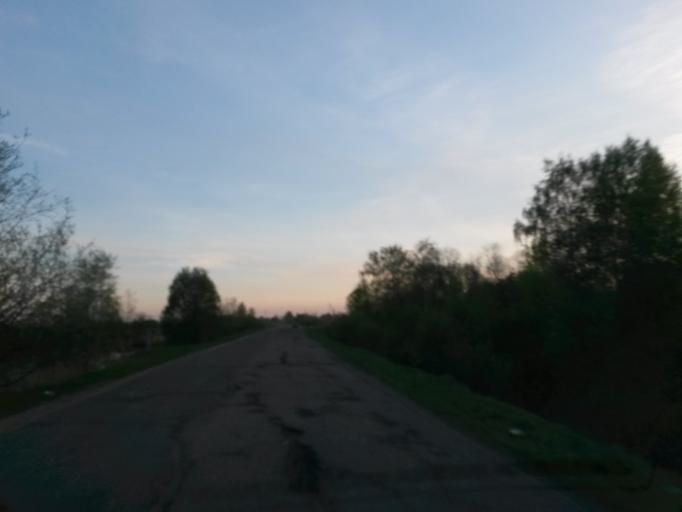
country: RU
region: Jaroslavl
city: Tutayev
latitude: 57.8969
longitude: 39.5706
